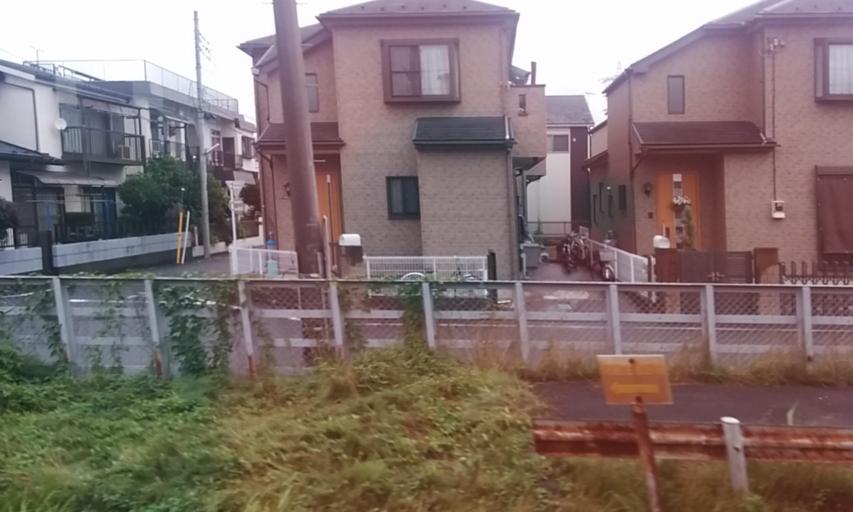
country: JP
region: Tokyo
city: Hachioji
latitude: 35.6506
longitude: 139.3484
